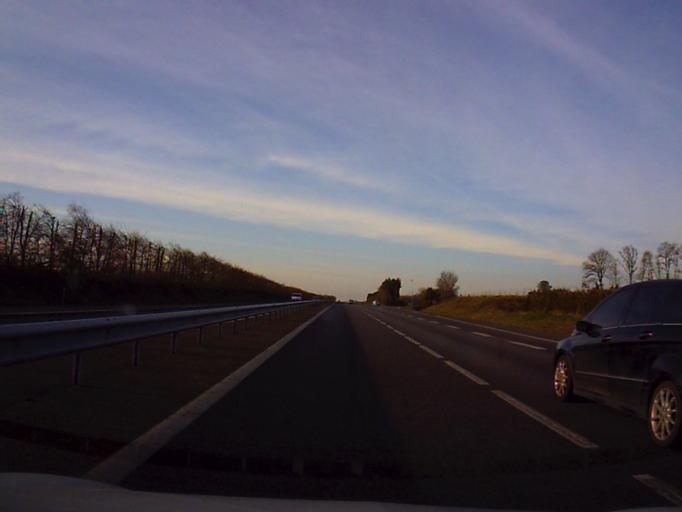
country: FR
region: Brittany
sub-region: Departement d'Ille-et-Vilaine
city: Plelan-le-Grand
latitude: 47.9700
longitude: -2.0959
